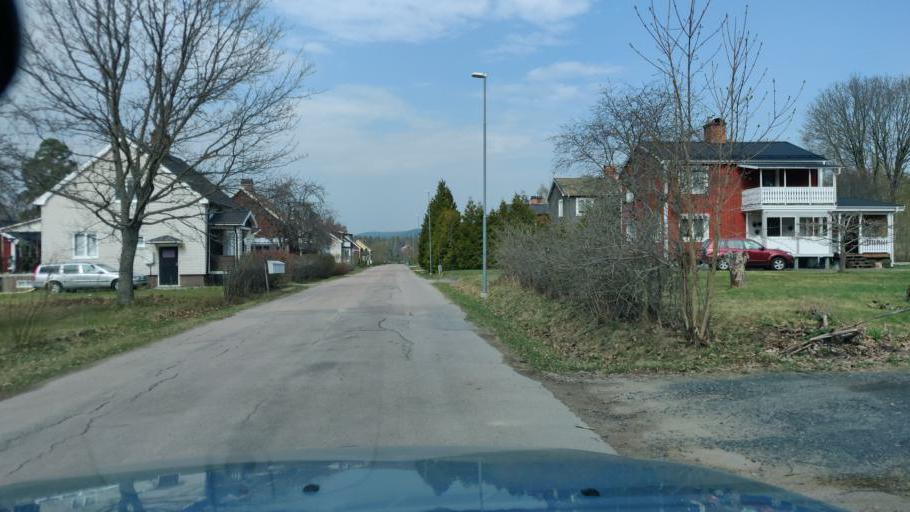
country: SE
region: Vaermland
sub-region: Munkfors Kommun
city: Munkfors
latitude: 59.8408
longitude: 13.5610
